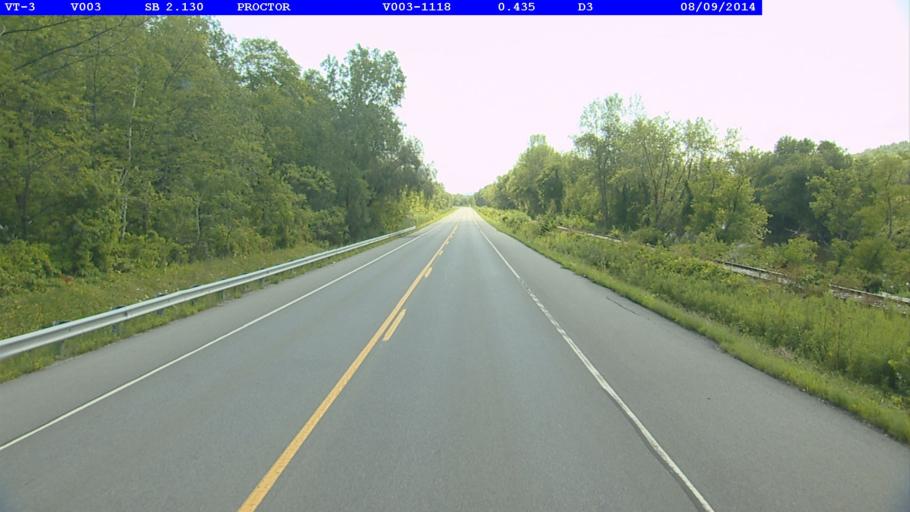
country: US
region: Vermont
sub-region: Rutland County
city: West Rutland
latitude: 43.6305
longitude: -73.0334
